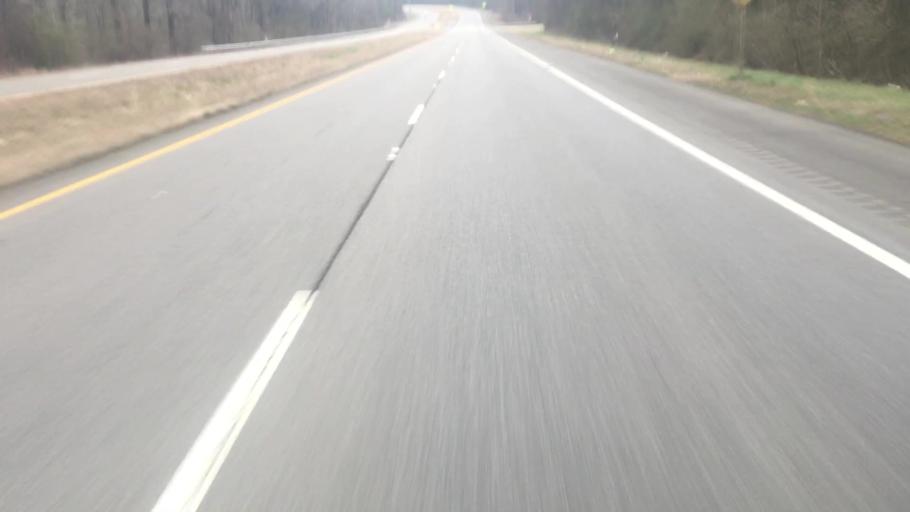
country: US
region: Alabama
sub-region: Walker County
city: Cordova
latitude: 33.8234
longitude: -87.1918
